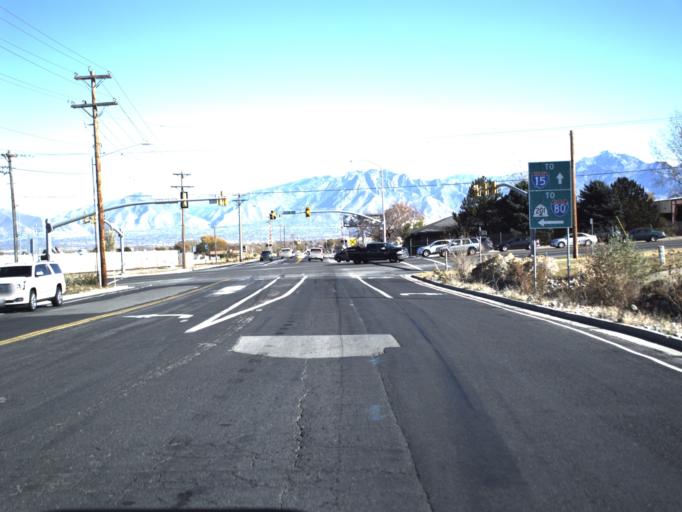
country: US
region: Utah
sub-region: Salt Lake County
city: Kearns
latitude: 40.6675
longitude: -112.0261
